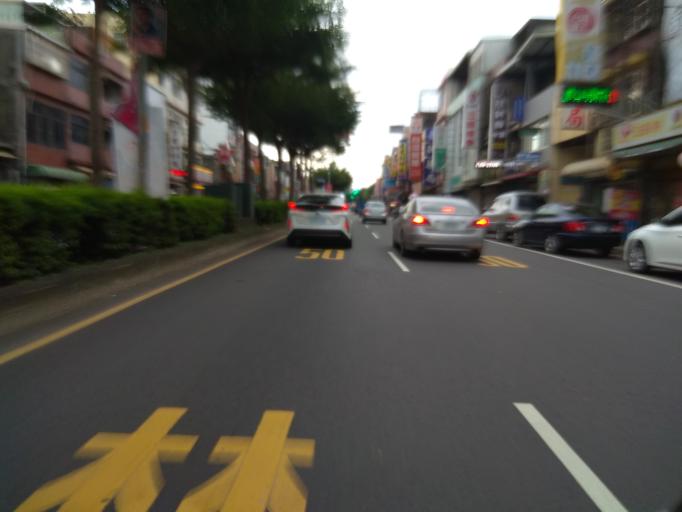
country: TW
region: Taiwan
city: Daxi
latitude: 24.8977
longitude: 121.2109
